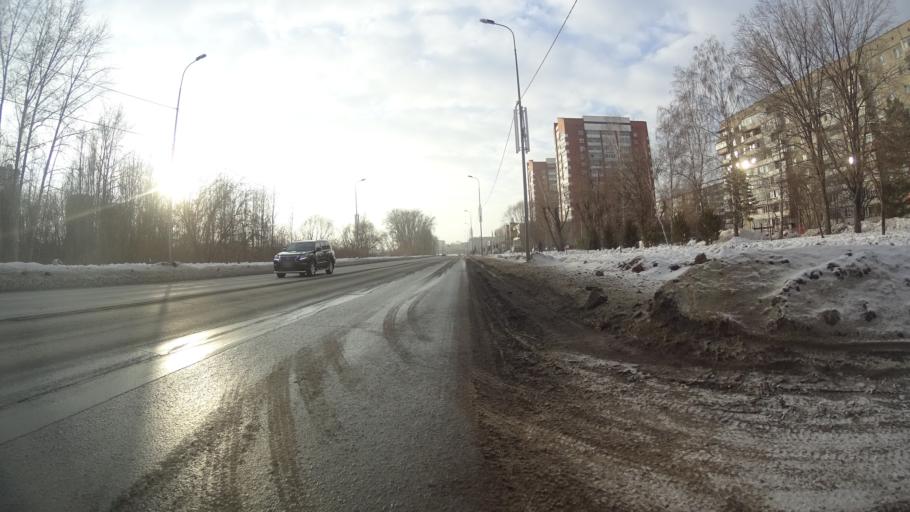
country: RU
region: Chelyabinsk
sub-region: Gorod Chelyabinsk
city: Chelyabinsk
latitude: 55.1759
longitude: 61.3658
